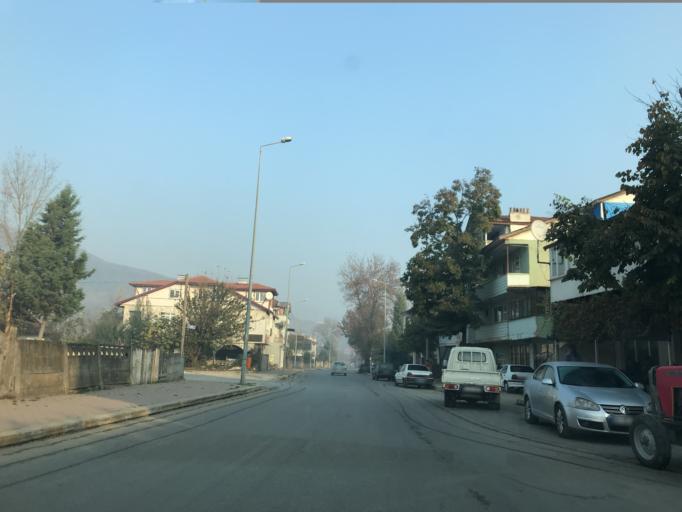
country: TR
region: Duzce
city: Cumayeri
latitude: 40.8815
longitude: 30.9513
